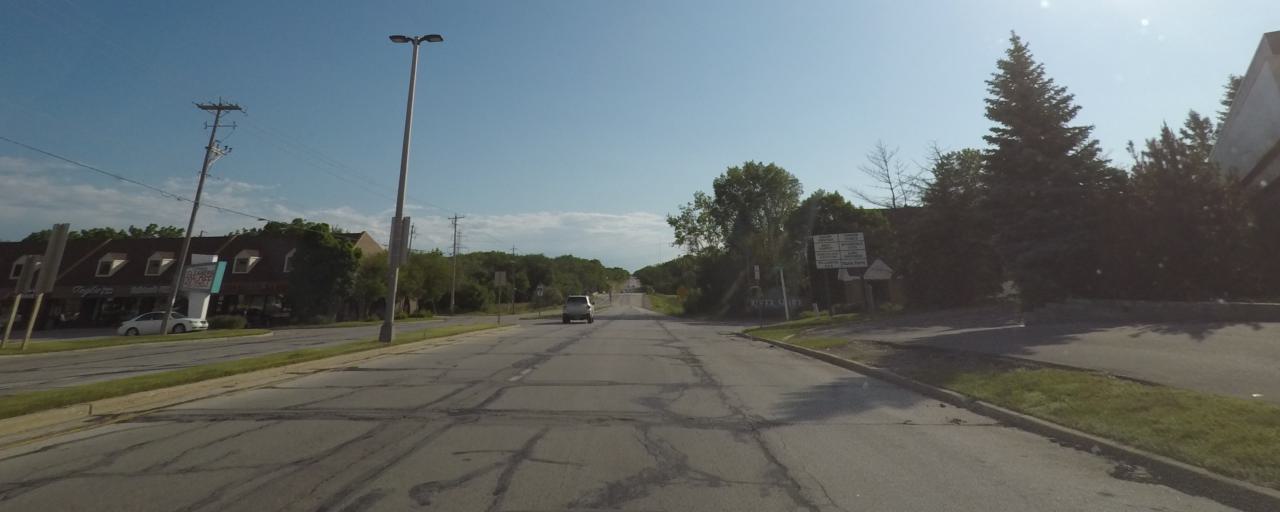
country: US
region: Wisconsin
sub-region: Milwaukee County
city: Hales Corners
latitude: 42.9752
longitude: -88.0480
